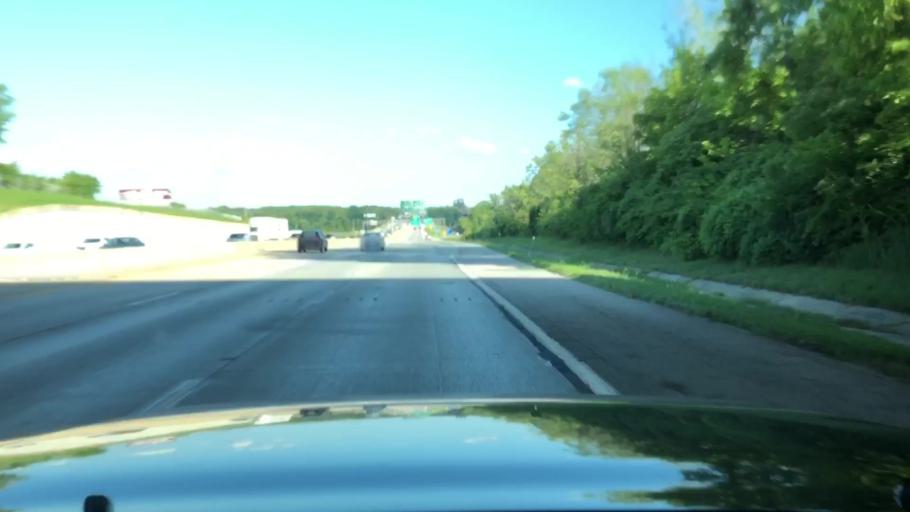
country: US
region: Missouri
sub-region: Saint Charles County
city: Saint Charles
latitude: 38.8072
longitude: -90.4809
